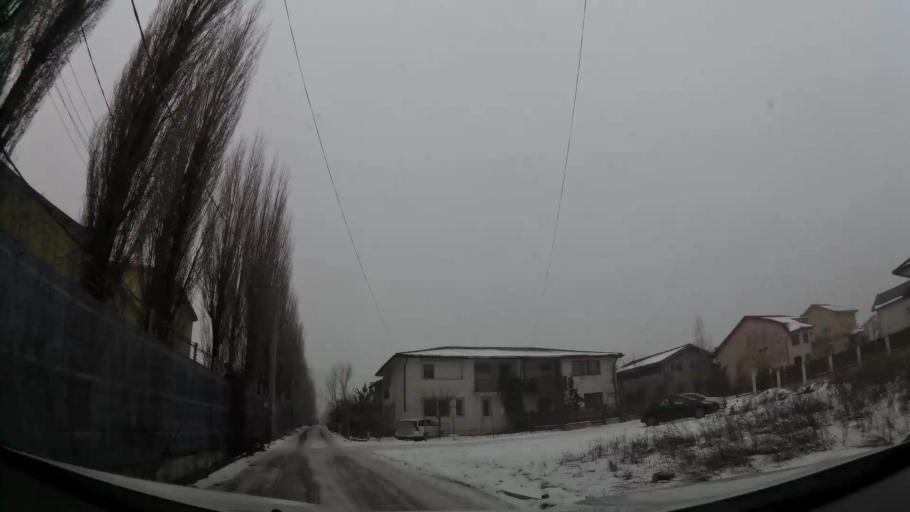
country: RO
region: Ilfov
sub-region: Comuna Chiajna
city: Rosu
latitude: 44.4445
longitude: 25.9996
